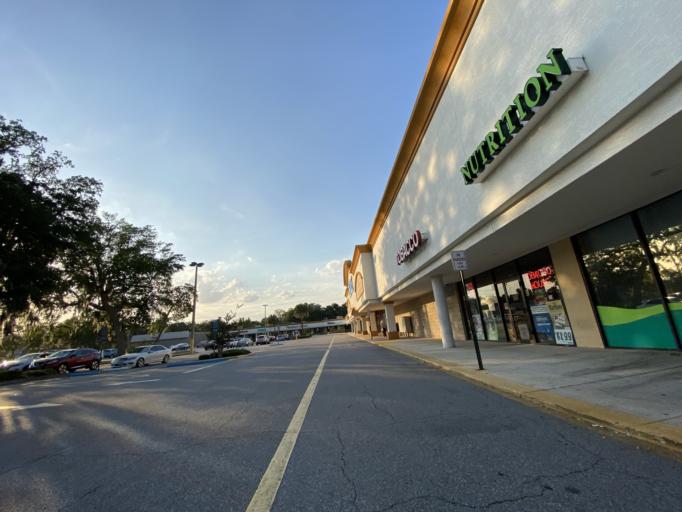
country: US
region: Florida
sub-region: Volusia County
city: Port Orange
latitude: 29.1304
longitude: -81.0053
